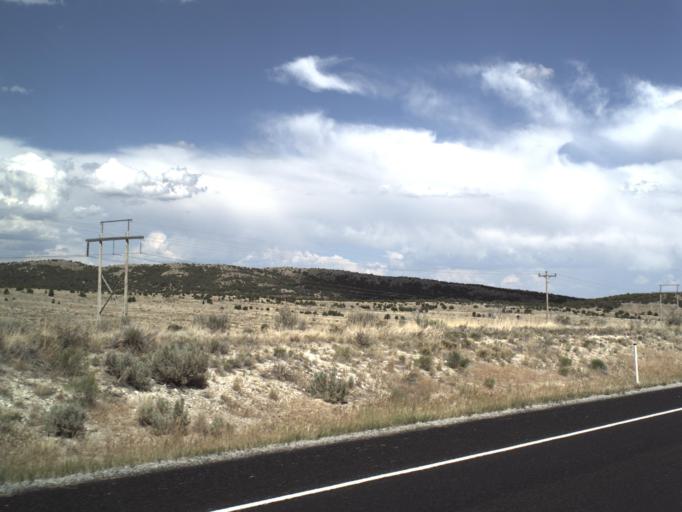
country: US
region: Idaho
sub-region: Minidoka County
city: Rupert
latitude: 41.9861
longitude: -113.1766
